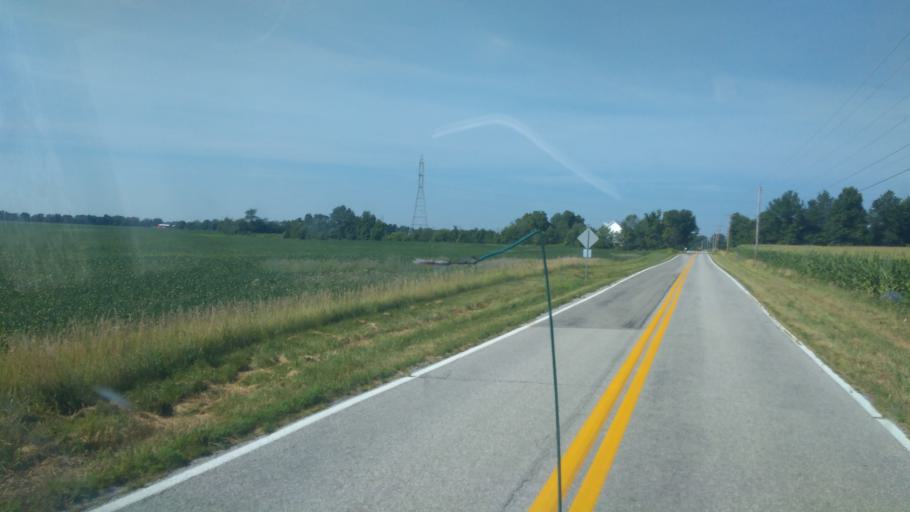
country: US
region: Ohio
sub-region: Union County
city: New California
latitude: 40.2915
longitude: -83.2111
